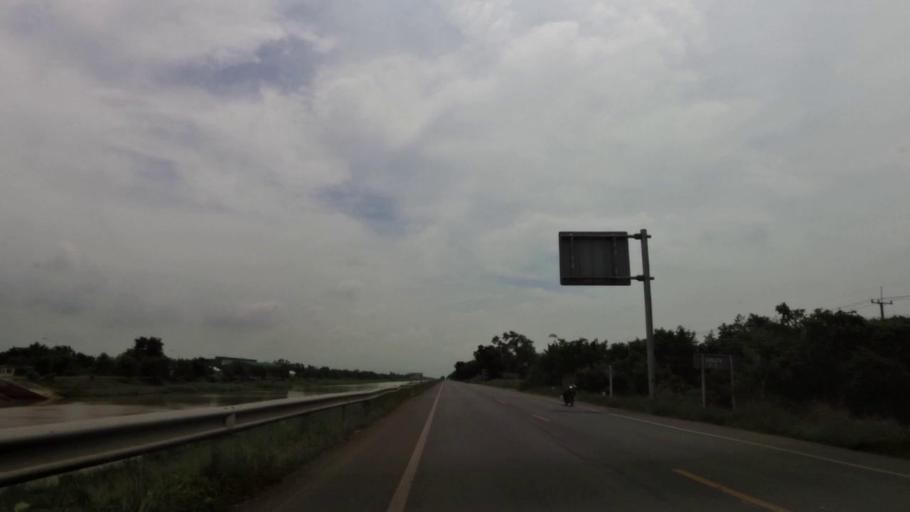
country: TH
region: Lop Buri
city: Ban Mi
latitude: 15.0445
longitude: 100.5644
